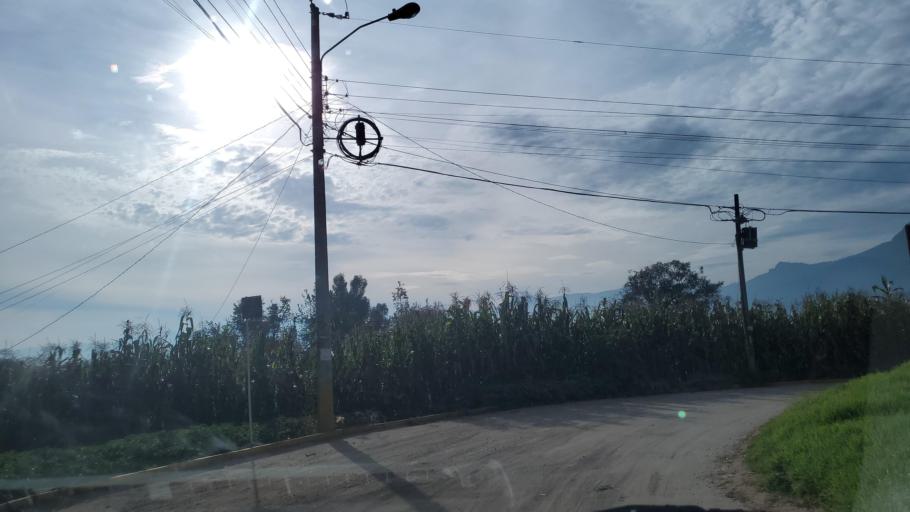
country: GT
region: Quetzaltenango
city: Quetzaltenango
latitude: 14.8424
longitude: -91.5467
